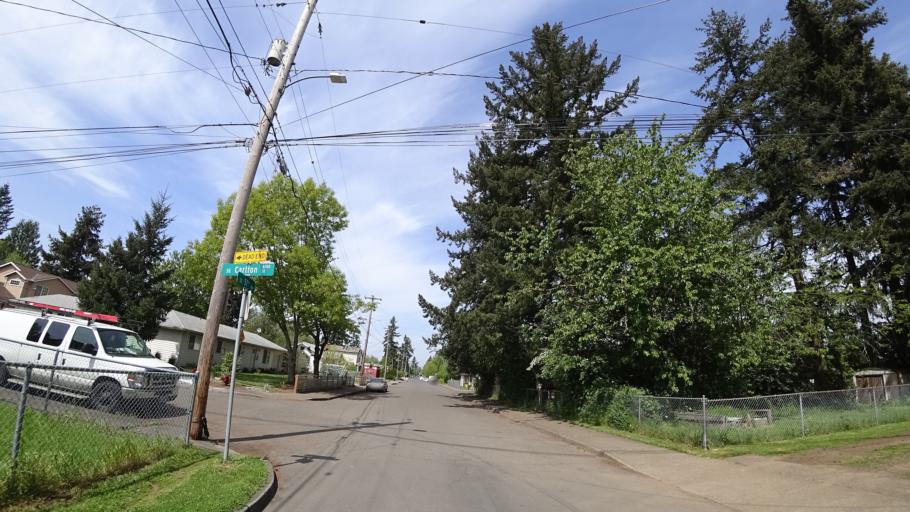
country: US
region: Oregon
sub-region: Multnomah County
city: Lents
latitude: 45.4778
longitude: -122.6048
